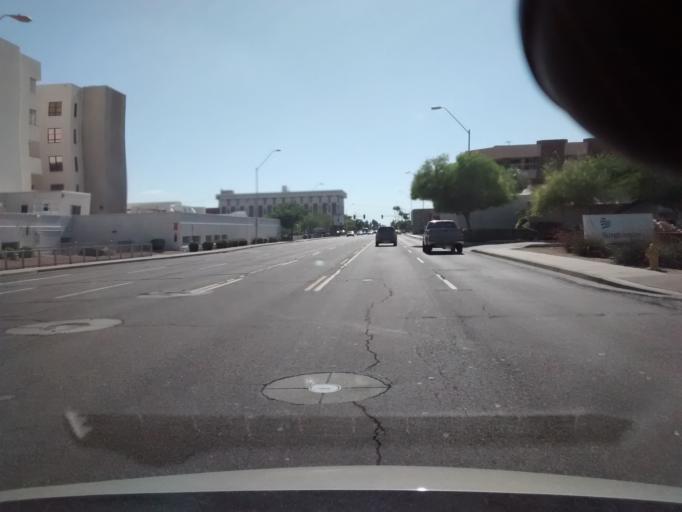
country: US
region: Arizona
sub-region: Maricopa County
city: Phoenix
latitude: 33.4658
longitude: -112.0585
